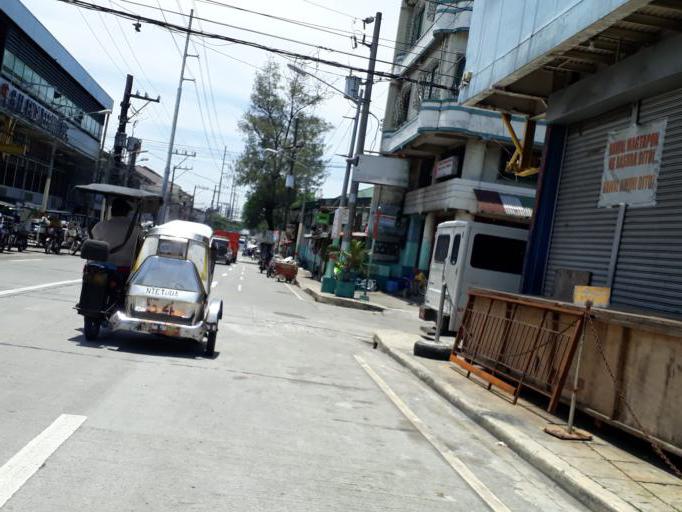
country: PH
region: Calabarzon
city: Del Monte
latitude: 14.6473
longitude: 120.9869
